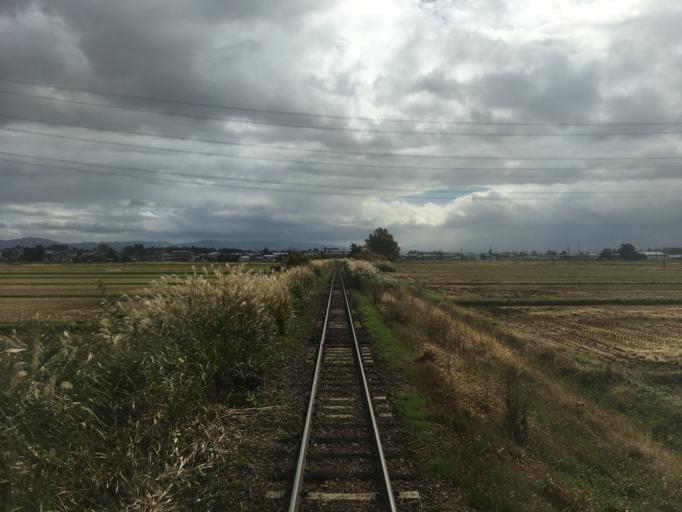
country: JP
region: Yamagata
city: Nagai
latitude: 38.0603
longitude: 140.0405
